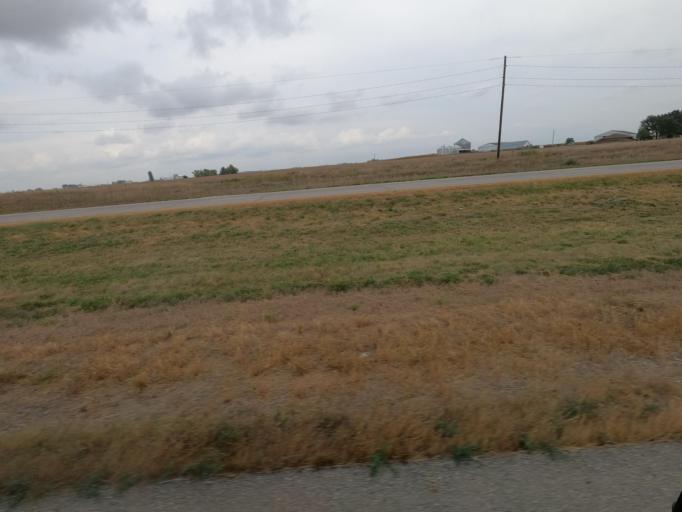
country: US
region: Iowa
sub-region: Jasper County
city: Monroe
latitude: 41.5551
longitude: -93.1426
